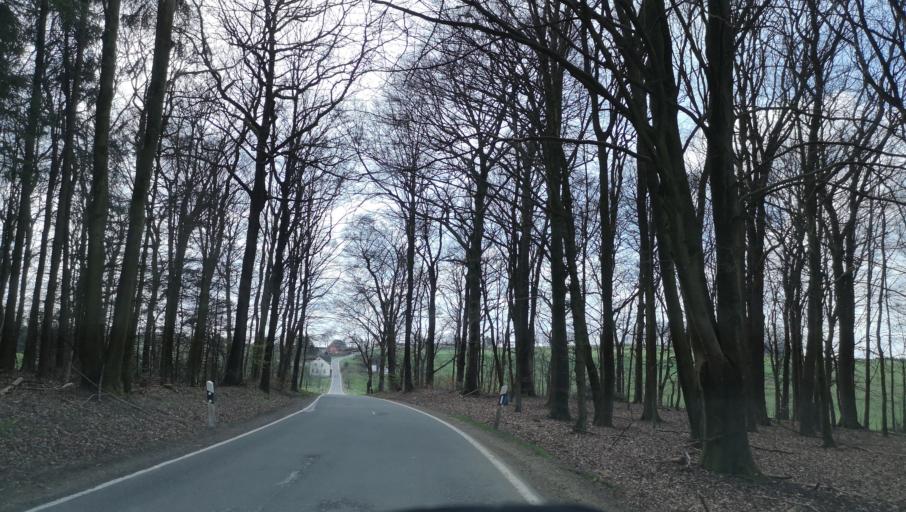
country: DE
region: North Rhine-Westphalia
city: Radevormwald
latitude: 51.2260
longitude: 7.3782
